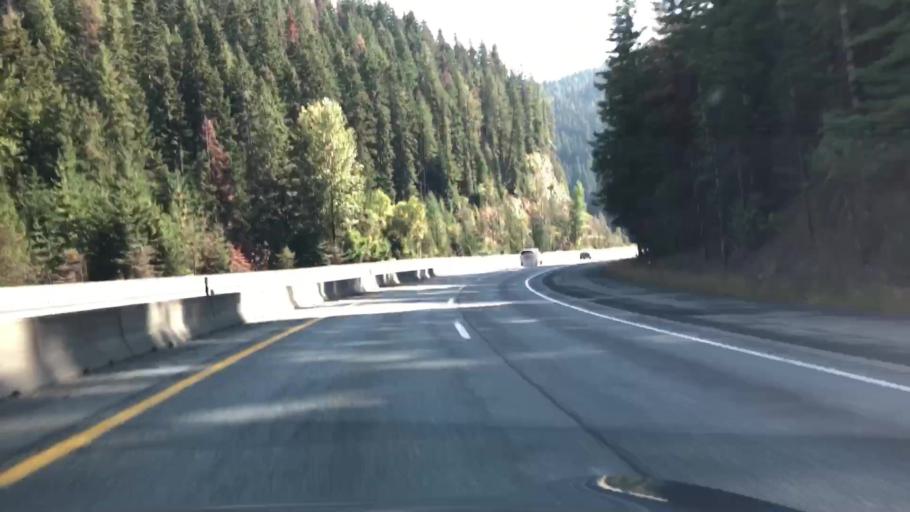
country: US
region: Idaho
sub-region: Shoshone County
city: Pinehurst
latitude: 47.5964
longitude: -116.4924
